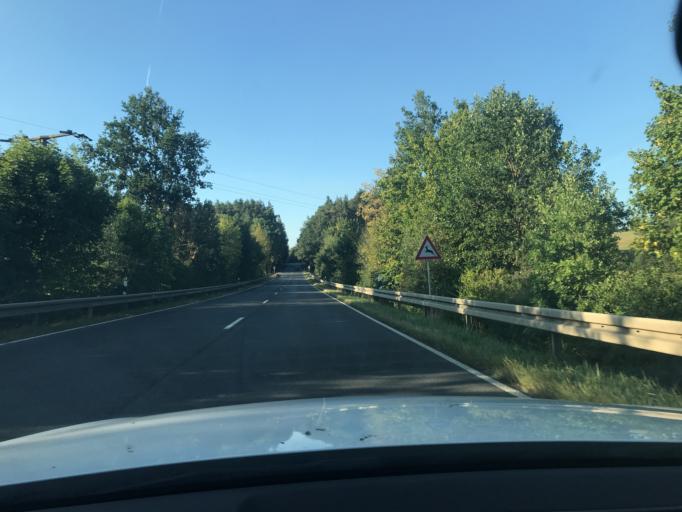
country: DE
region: Bavaria
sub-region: Upper Franconia
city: Emtmannsberg
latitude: 49.8864
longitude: 11.6114
